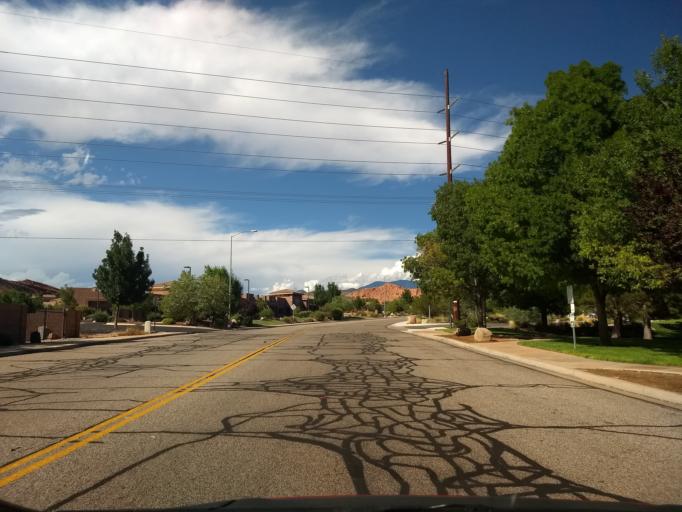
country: US
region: Utah
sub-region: Washington County
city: Santa Clara
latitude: 37.1318
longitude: -113.6140
